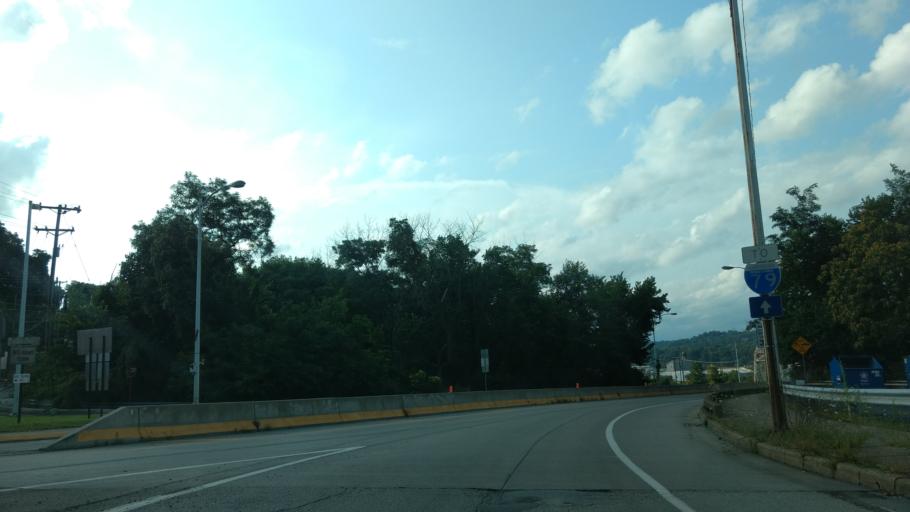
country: US
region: Pennsylvania
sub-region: Allegheny County
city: Avalon
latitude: 40.4892
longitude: -80.0797
